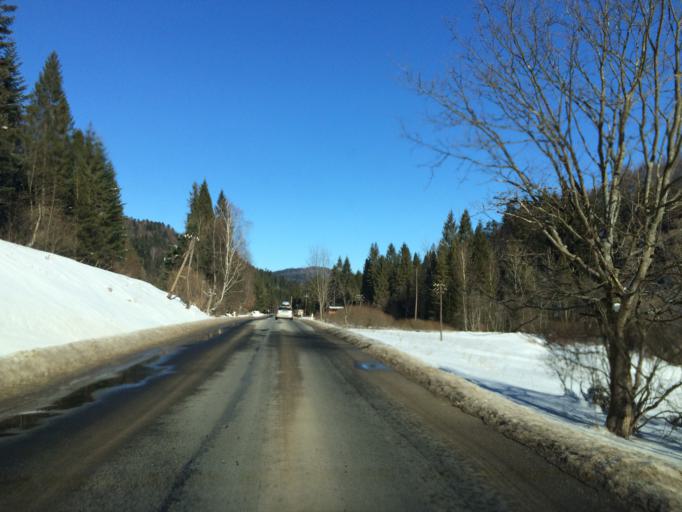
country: PL
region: Subcarpathian Voivodeship
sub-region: Powiat leski
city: Cisna
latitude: 49.2085
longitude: 22.3634
